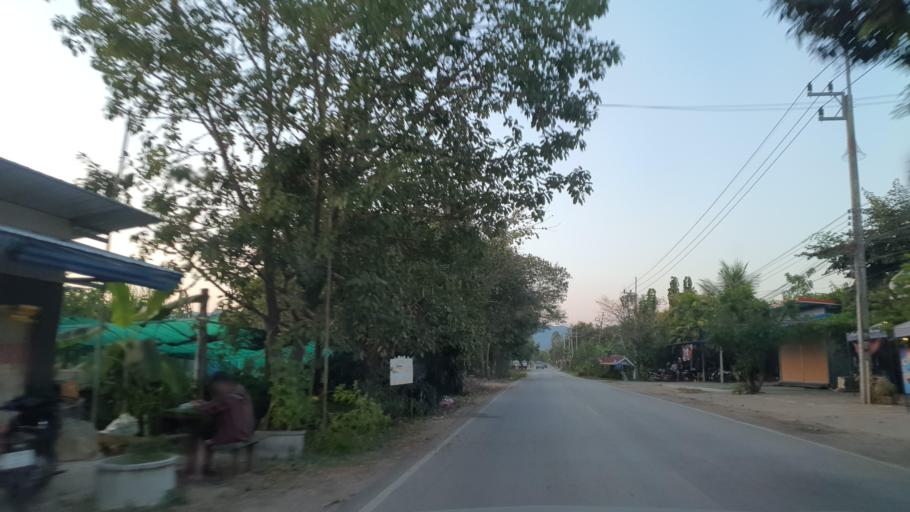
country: TH
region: Chiang Mai
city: Mae Wang
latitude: 18.6341
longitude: 98.8015
